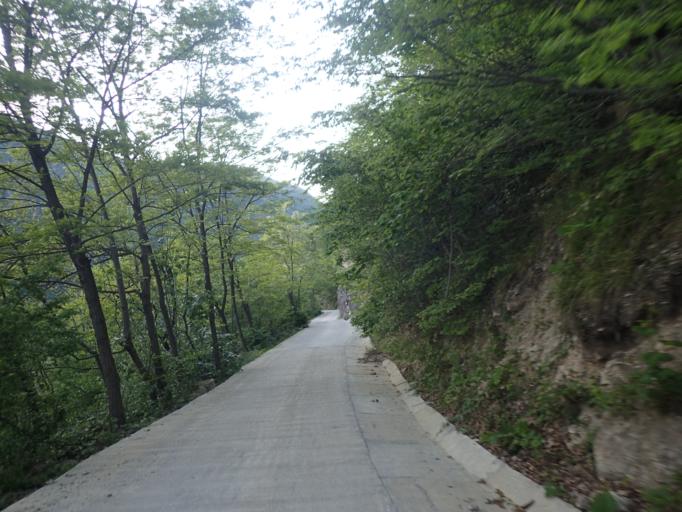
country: TR
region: Ordu
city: Kabaduz
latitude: 40.7921
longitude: 37.8750
